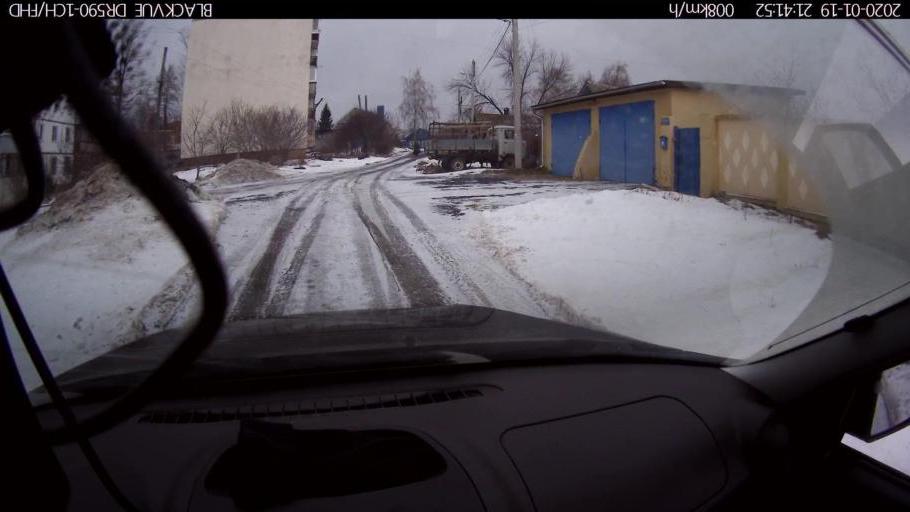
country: RU
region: Nizjnij Novgorod
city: Nizhniy Novgorod
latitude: 56.2332
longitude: 43.9782
